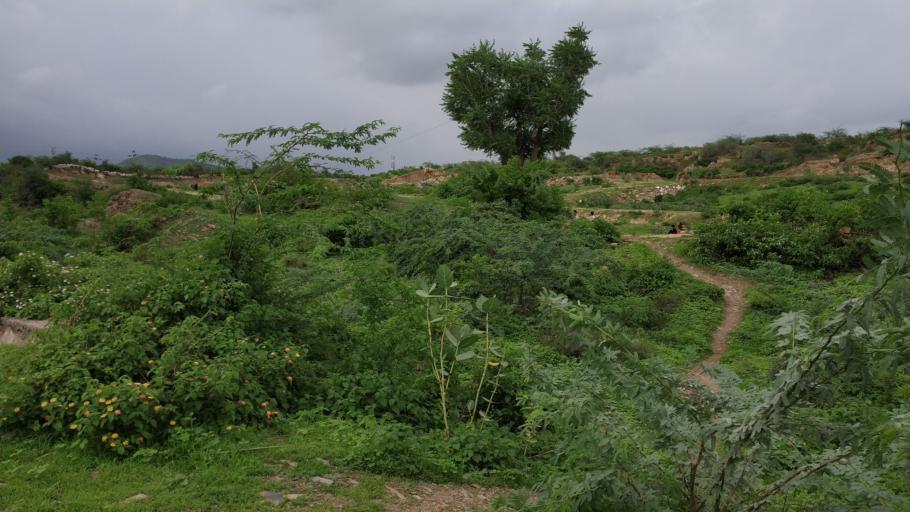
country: IN
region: Rajasthan
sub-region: Udaipur
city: Udaipur
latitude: 24.5929
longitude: 73.6543
